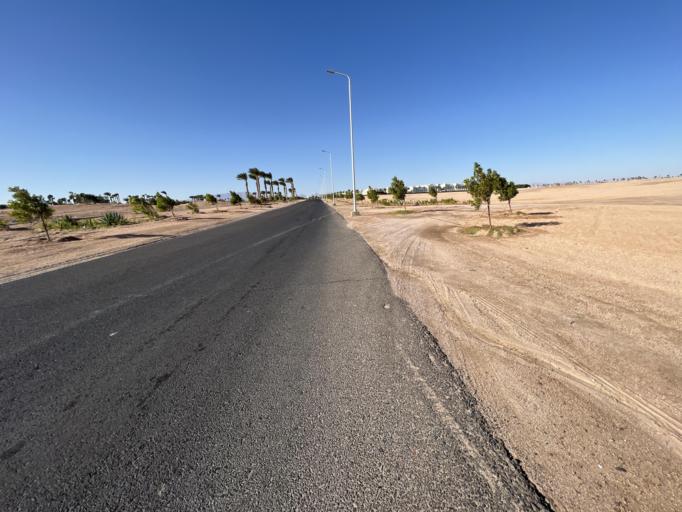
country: EG
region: Red Sea
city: Makadi Bay
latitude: 26.9840
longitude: 33.8796
